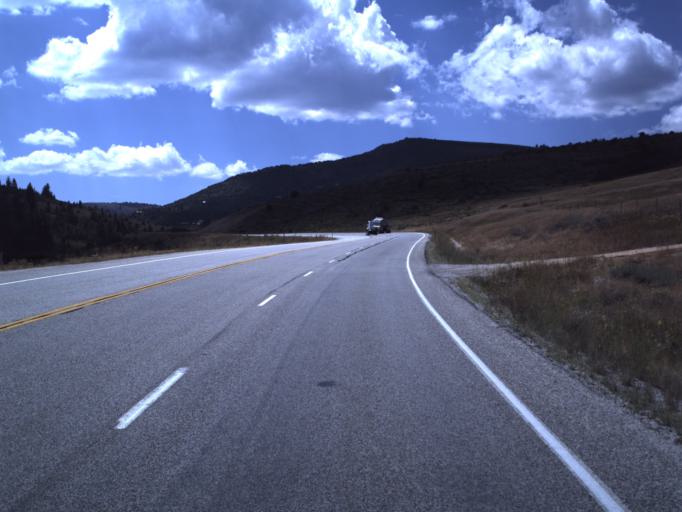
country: US
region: Idaho
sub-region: Bear Lake County
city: Paris
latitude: 41.9347
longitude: -111.4138
